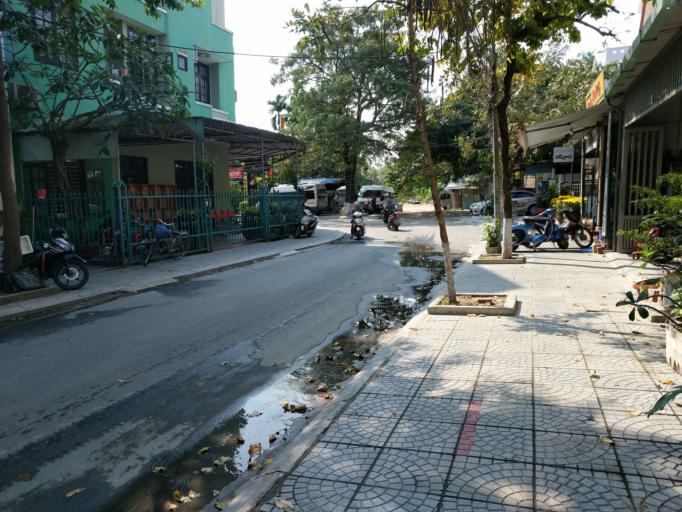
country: VN
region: Quang Nam
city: Hoi An
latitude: 15.8833
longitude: 108.3249
